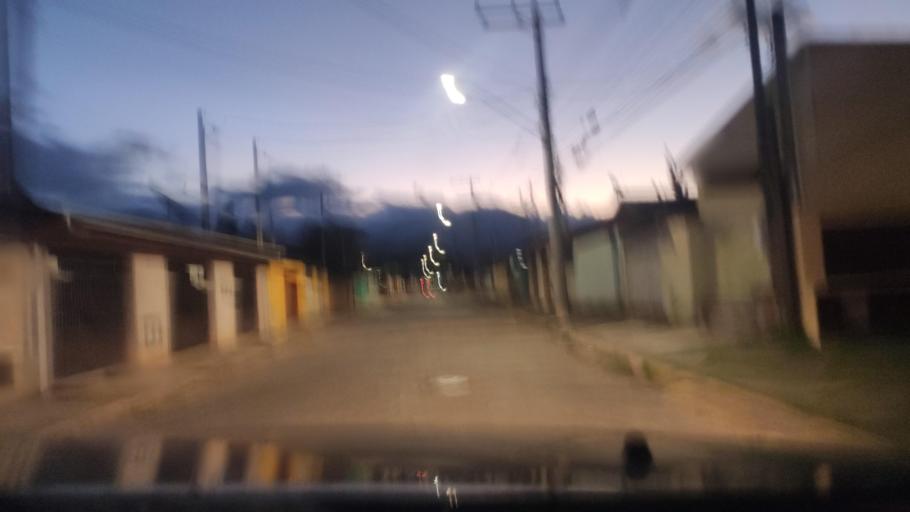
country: BR
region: Minas Gerais
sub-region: Paraisopolis
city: Paraisopolis
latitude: -22.6923
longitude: -45.7412
